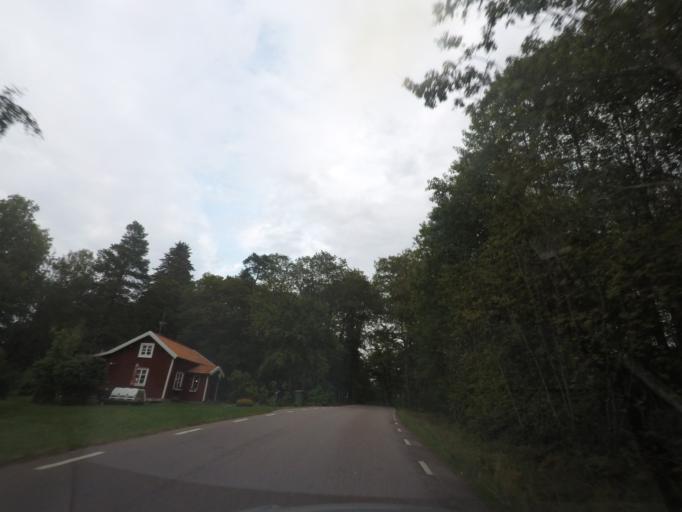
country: SE
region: Vaestmanland
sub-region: Hallstahammars Kommun
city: Kolback
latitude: 59.5278
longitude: 16.2252
